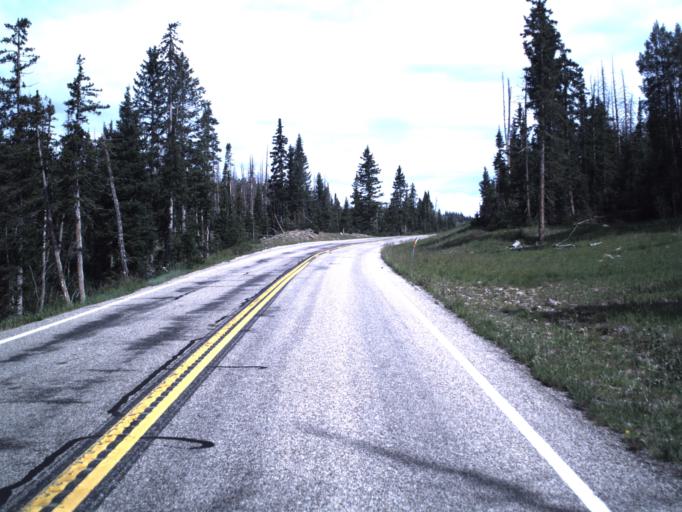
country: US
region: Utah
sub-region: Iron County
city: Cedar City
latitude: 37.5845
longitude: -112.8468
